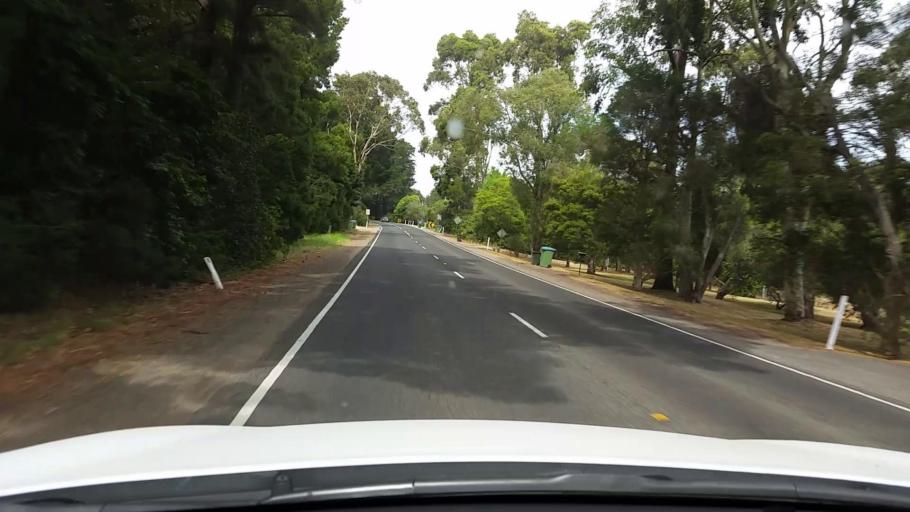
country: AU
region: Victoria
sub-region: Mornington Peninsula
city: Merricks
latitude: -38.3919
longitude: 145.0864
